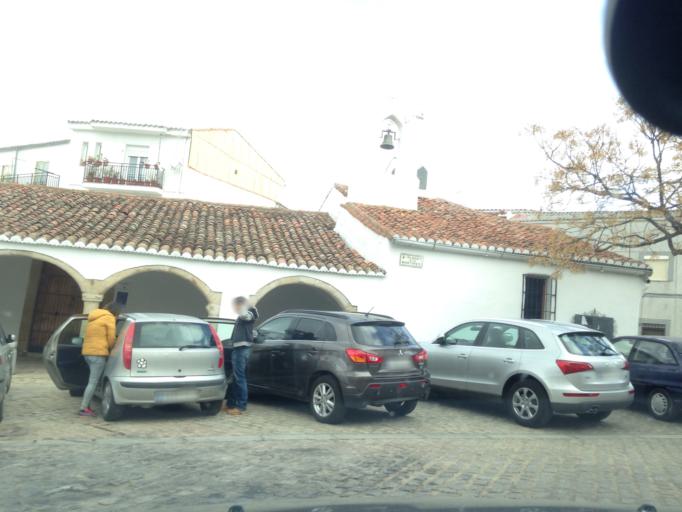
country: ES
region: Extremadura
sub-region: Provincia de Caceres
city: Montanchez
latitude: 39.2265
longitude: -6.1500
